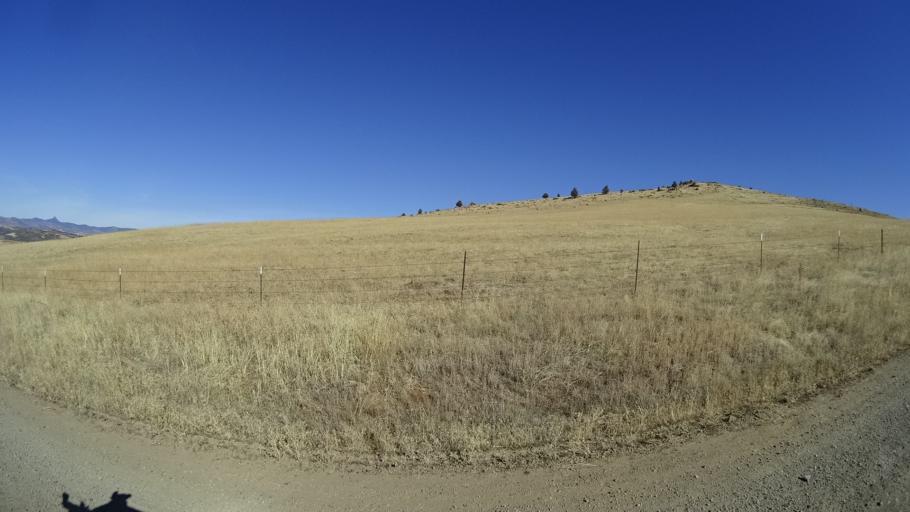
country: US
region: California
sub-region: Siskiyou County
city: Montague
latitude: 41.8446
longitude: -122.4298
